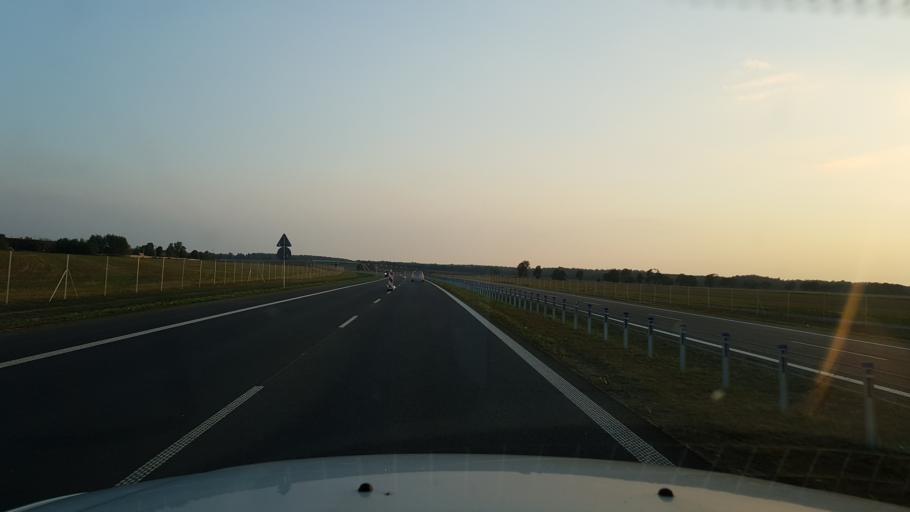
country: PL
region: West Pomeranian Voivodeship
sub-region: Powiat gryficki
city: Ploty
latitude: 53.7793
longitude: 15.2431
